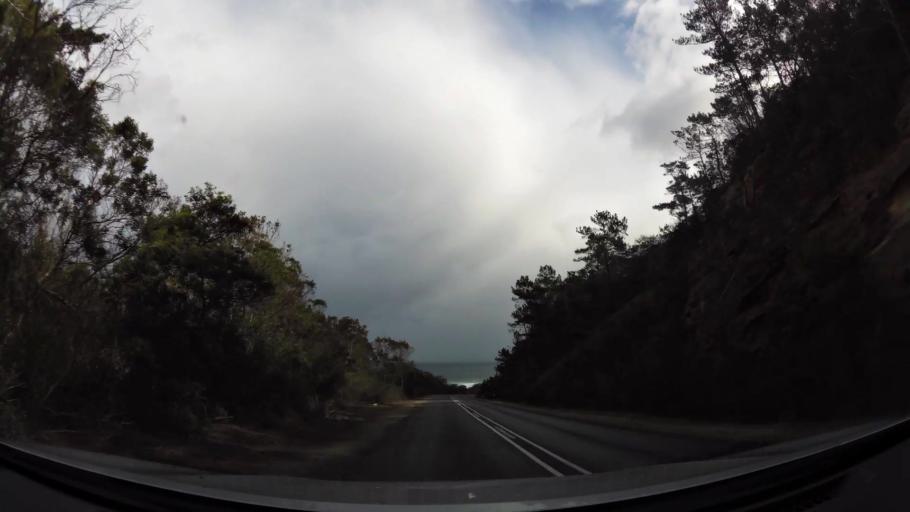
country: ZA
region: Western Cape
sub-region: Eden District Municipality
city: George
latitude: -34.0450
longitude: 22.3191
